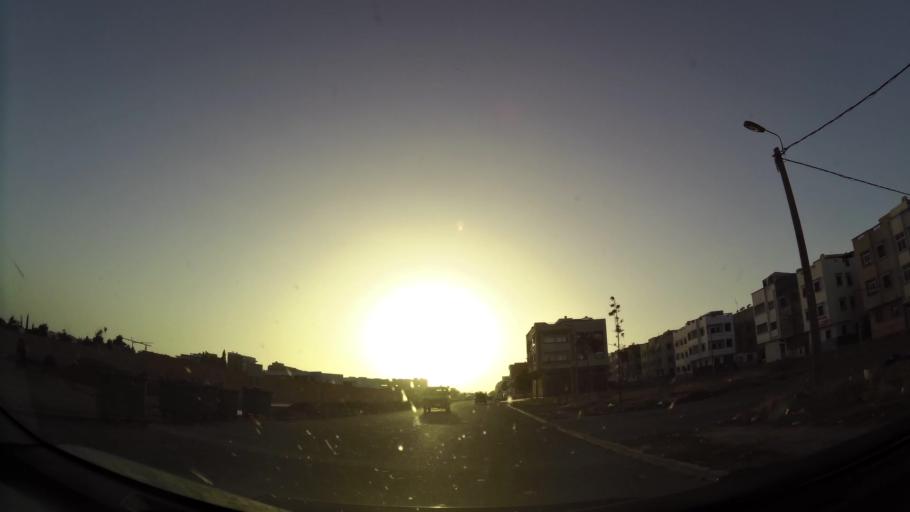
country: MA
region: Oued ed Dahab-Lagouira
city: Dakhla
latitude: 30.3956
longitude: -9.5624
